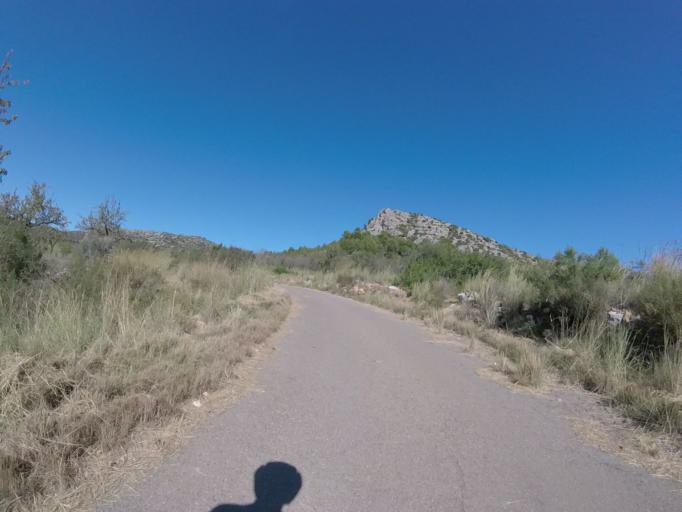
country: ES
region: Valencia
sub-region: Provincia de Castello
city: Orpesa/Oropesa del Mar
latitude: 40.1363
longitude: 0.1049
